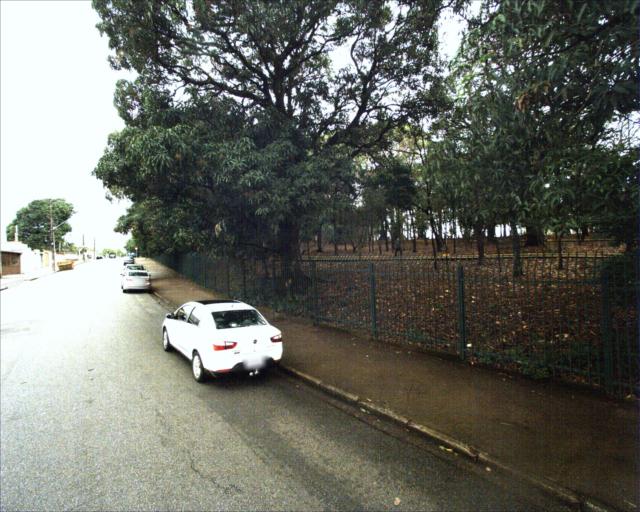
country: BR
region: Sao Paulo
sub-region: Sorocaba
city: Sorocaba
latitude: -23.4877
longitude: -47.4715
